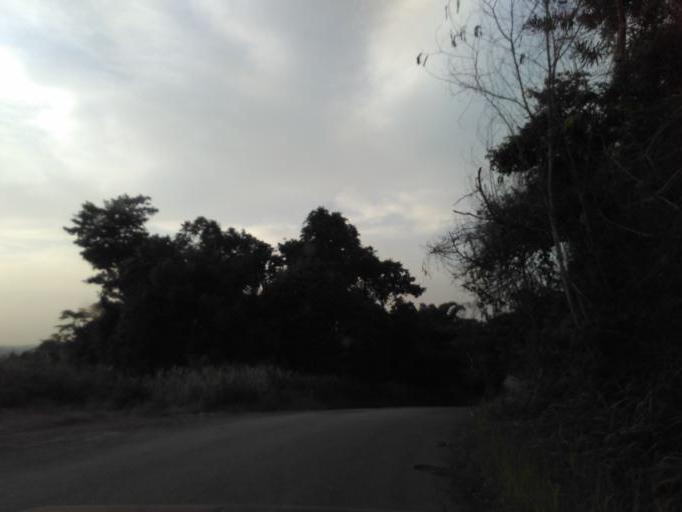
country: GH
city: Bekwai
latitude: 6.5431
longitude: -1.4401
